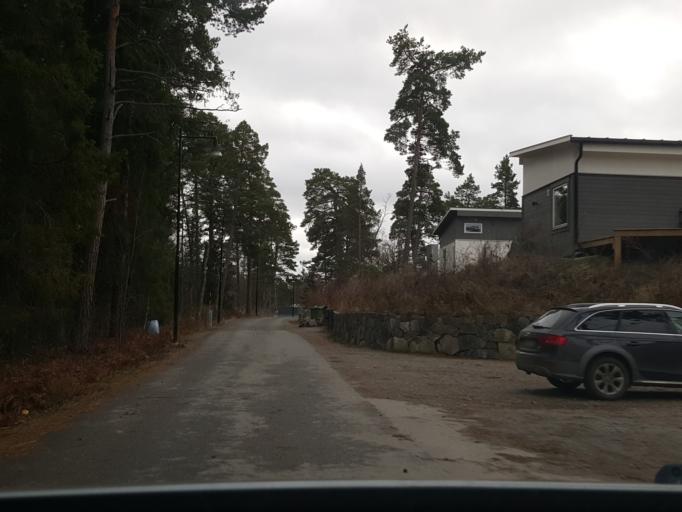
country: SE
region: Stockholm
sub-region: Nacka Kommun
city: Boo
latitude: 59.3243
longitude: 18.2862
